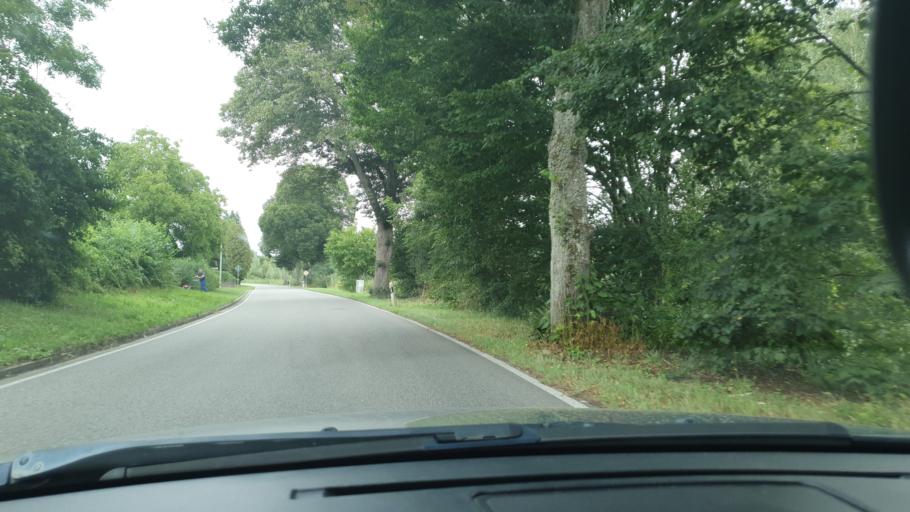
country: DE
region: Rheinland-Pfalz
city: Rieschweiler-Muhlbach
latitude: 49.2426
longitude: 7.4957
